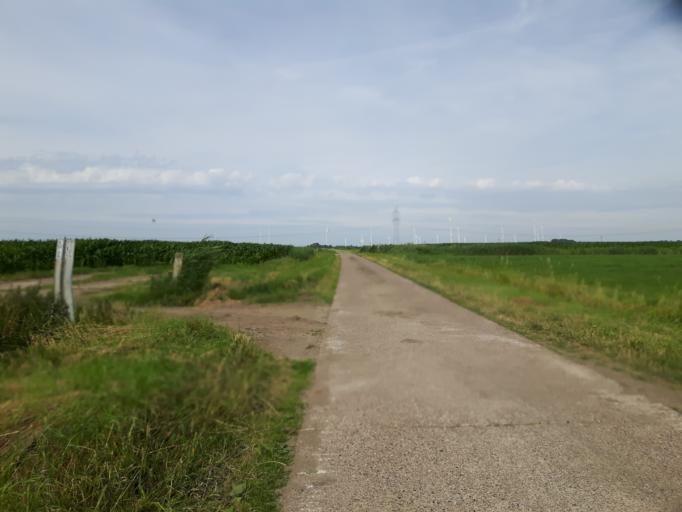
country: DE
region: Lower Saxony
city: Elsfleth
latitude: 53.2601
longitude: 8.4279
